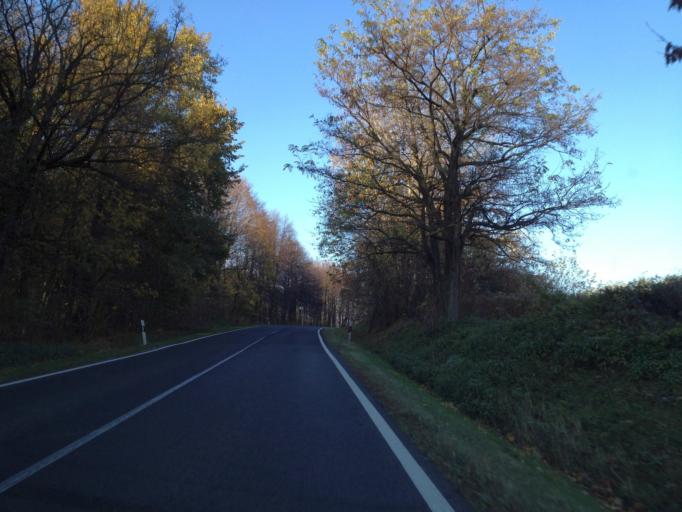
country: HU
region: Veszprem
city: Zirc
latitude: 47.3193
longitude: 17.8763
